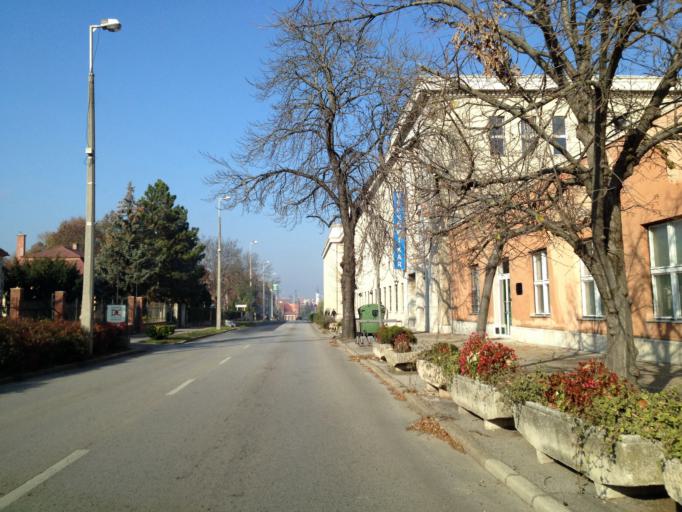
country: HU
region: Veszprem
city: Veszprem
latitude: 47.0867
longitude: 17.9085
